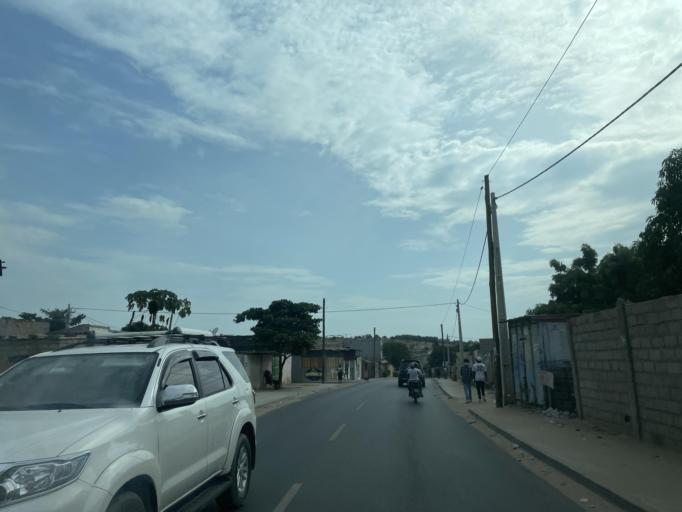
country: AO
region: Luanda
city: Luanda
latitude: -8.9336
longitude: 13.1995
